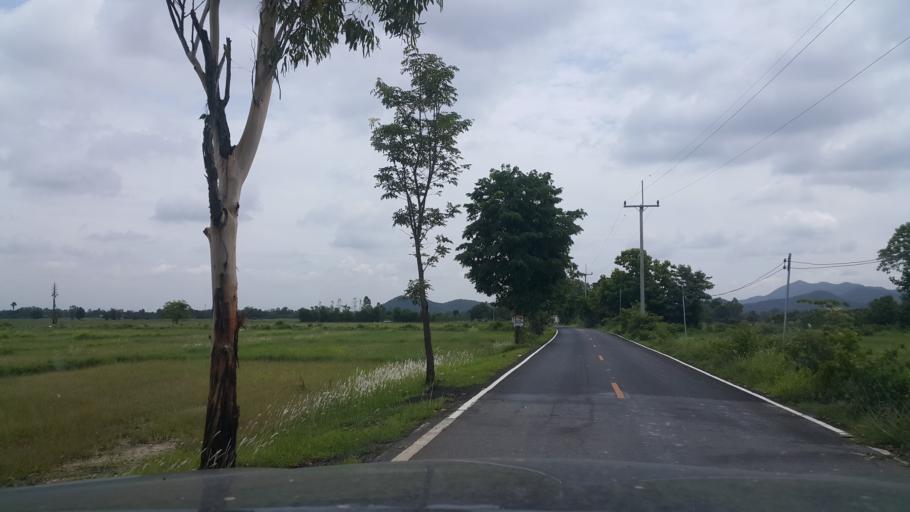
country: TH
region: Lamphun
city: Ban Thi
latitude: 18.6485
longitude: 99.1468
